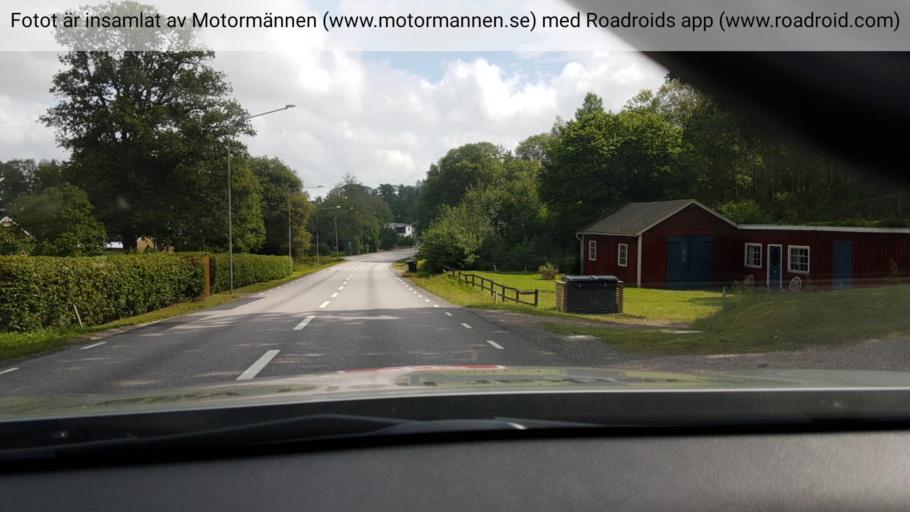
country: SE
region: Vaestra Goetaland
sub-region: Svenljunga Kommun
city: Svenljunga
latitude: 57.4991
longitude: 13.0972
